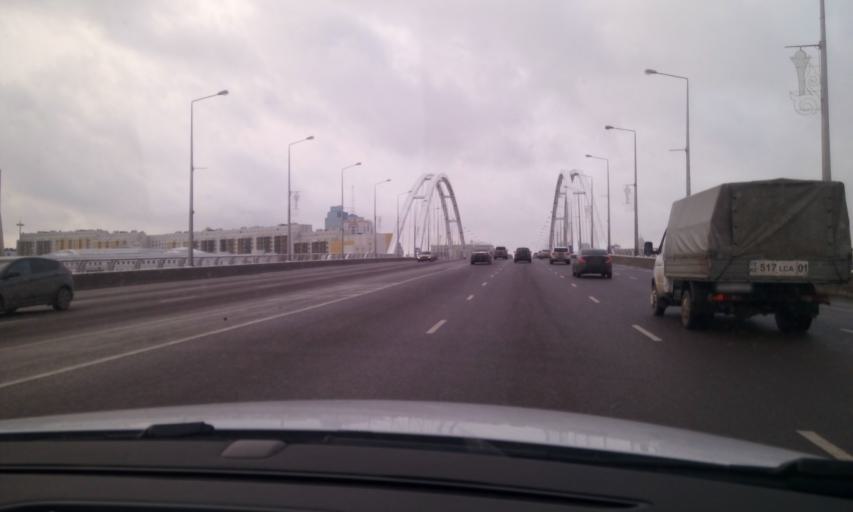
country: KZ
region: Astana Qalasy
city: Astana
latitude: 51.1307
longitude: 71.4506
